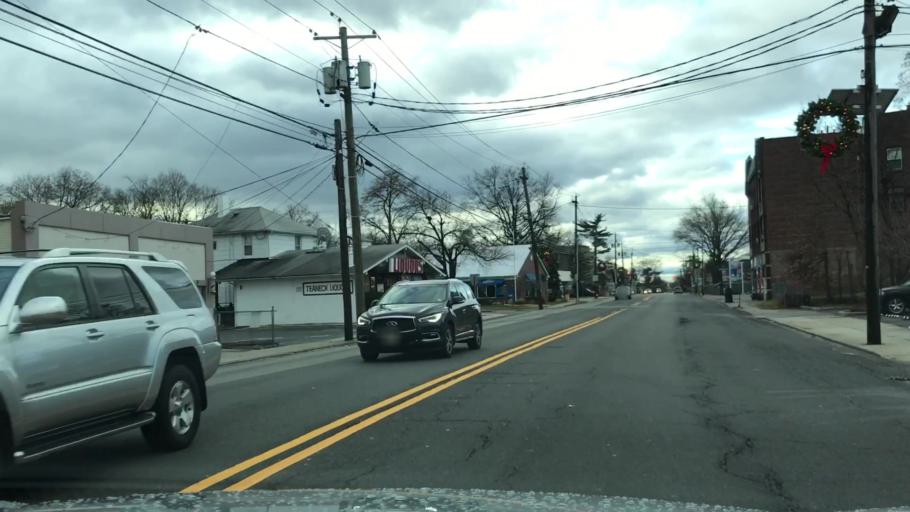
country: US
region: New Jersey
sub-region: Bergen County
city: Teaneck
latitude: 40.9037
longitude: -73.9987
